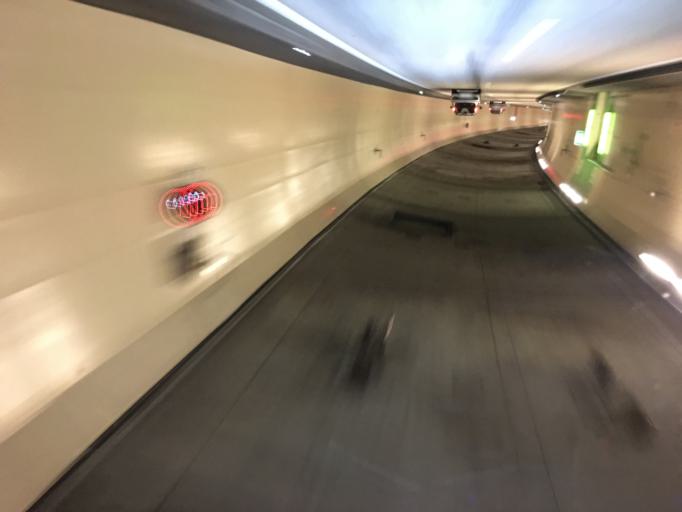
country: CH
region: Nidwalden
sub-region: Nidwalden
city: Stansstad
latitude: 46.9792
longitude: 8.3290
